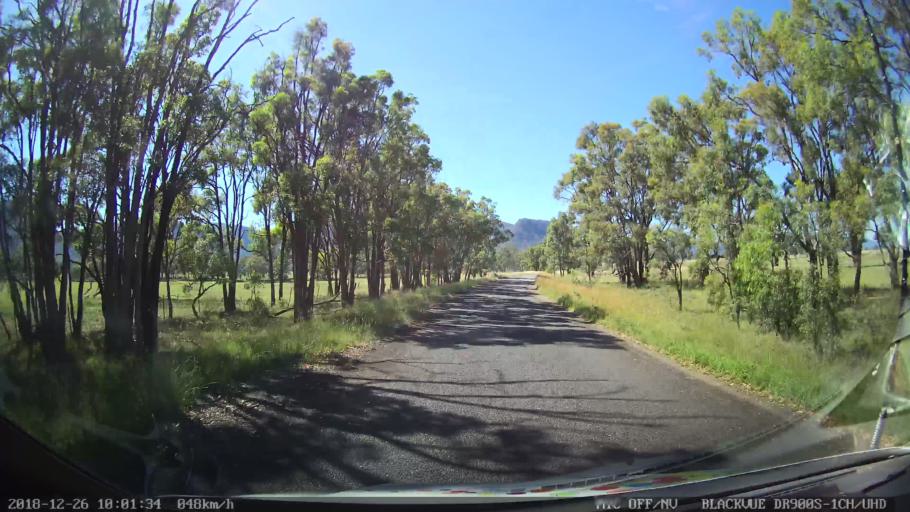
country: AU
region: New South Wales
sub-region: Mid-Western Regional
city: Kandos
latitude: -33.0480
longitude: 150.2221
